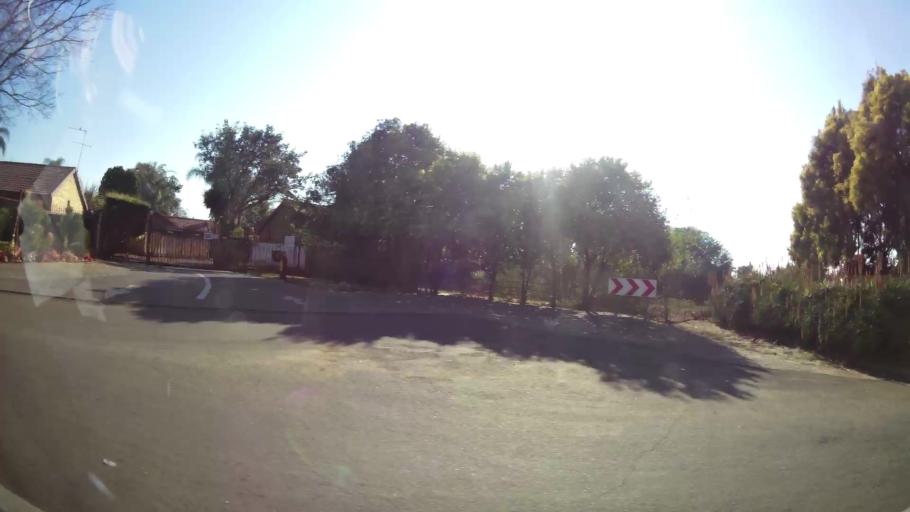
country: ZA
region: Gauteng
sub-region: City of Tshwane Metropolitan Municipality
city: Pretoria
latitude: -25.6497
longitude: 28.2475
